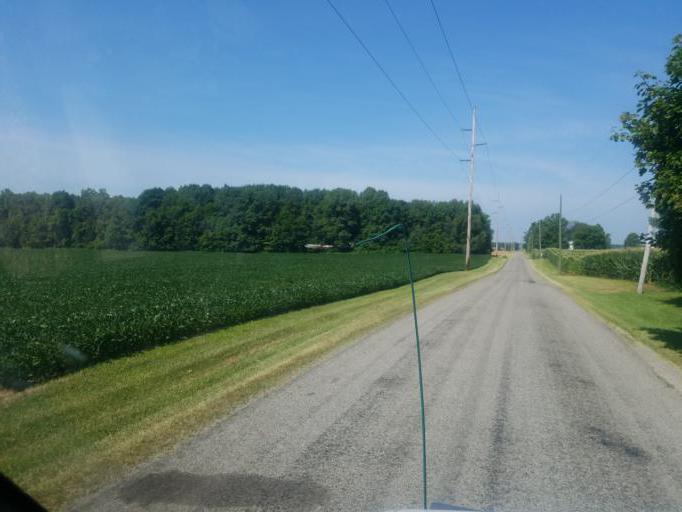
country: US
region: Ohio
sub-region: Union County
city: Marysville
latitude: 40.2878
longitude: -83.3678
